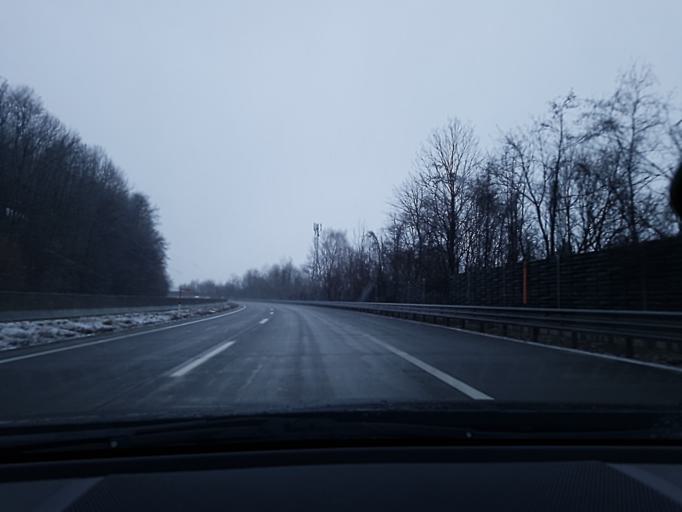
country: AT
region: Salzburg
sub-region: Politischer Bezirk Hallein
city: Kuchl
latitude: 47.6197
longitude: 13.1390
